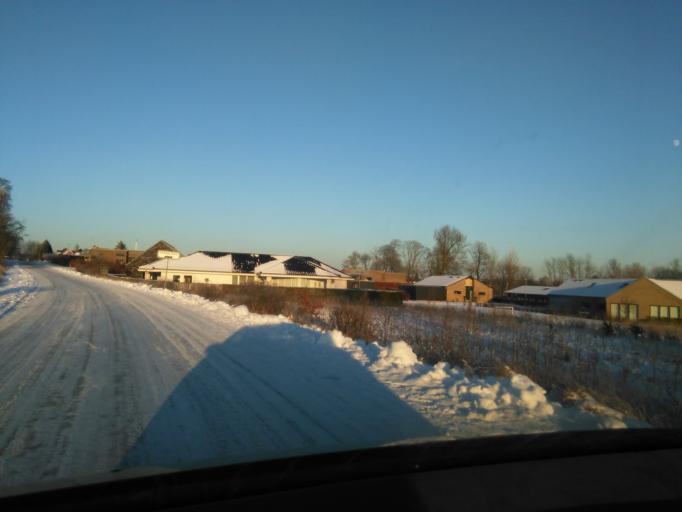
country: DK
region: Central Jutland
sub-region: Arhus Kommune
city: Tranbjerg
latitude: 56.0803
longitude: 10.1202
